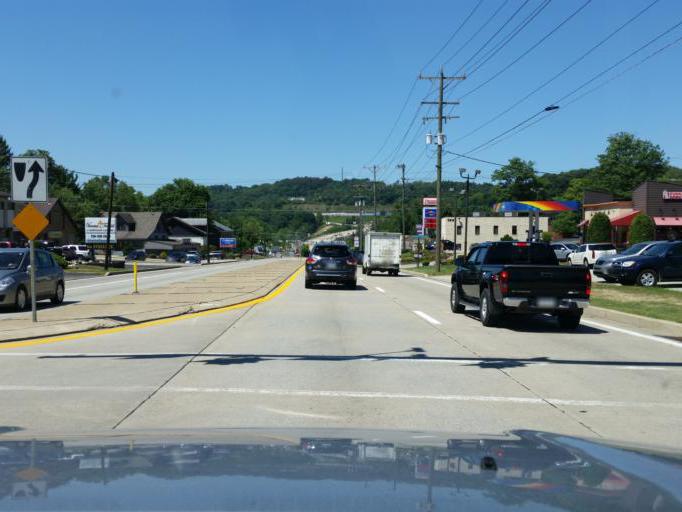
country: US
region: Pennsylvania
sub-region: Westmoreland County
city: Murrysville
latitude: 40.4274
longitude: -79.6938
